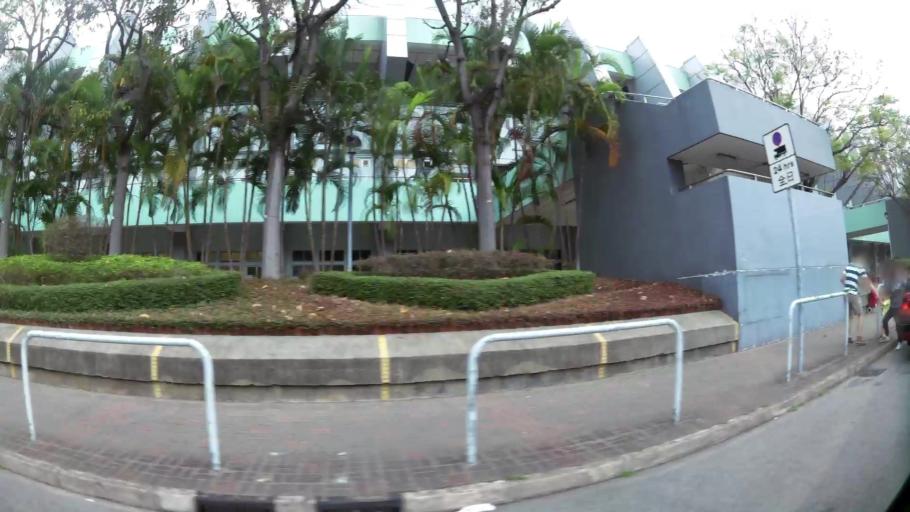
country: HK
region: Kowloon City
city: Kowloon
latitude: 22.3264
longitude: 114.2097
